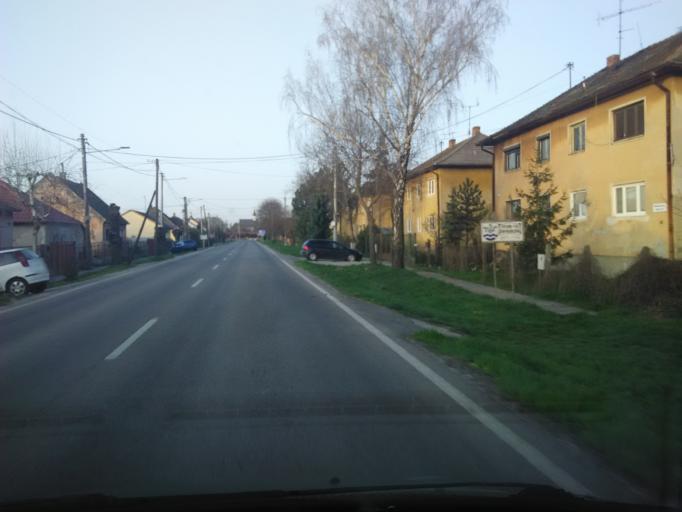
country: SK
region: Nitriansky
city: Sellye
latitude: 48.1561
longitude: 17.9318
